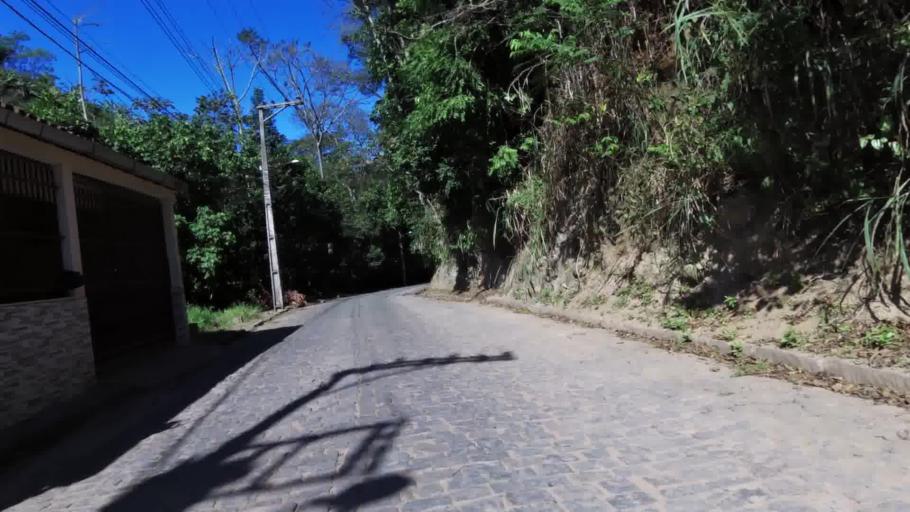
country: BR
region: Espirito Santo
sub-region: Rio Novo Do Sul
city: Rio Novo do Sul
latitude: -20.8539
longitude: -40.9240
